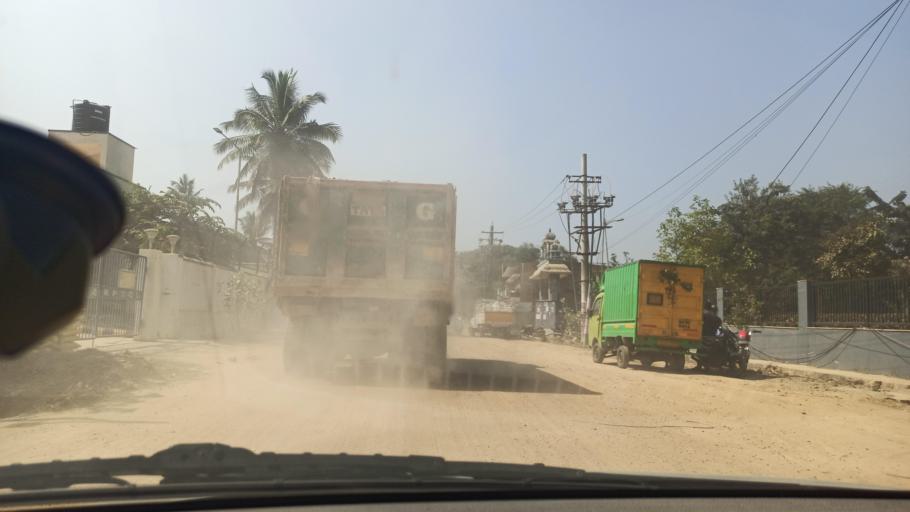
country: IN
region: Karnataka
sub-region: Bangalore Urban
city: Bangalore
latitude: 12.9393
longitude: 77.6889
